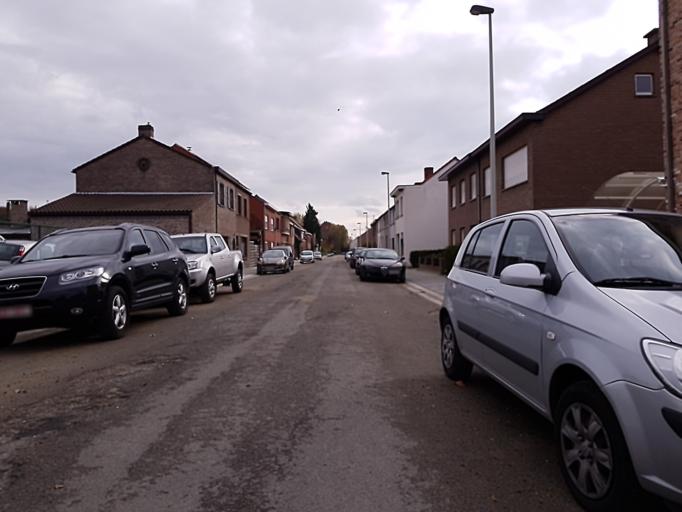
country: BE
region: Flanders
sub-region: Provincie Antwerpen
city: Ranst
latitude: 51.1871
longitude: 4.5650
